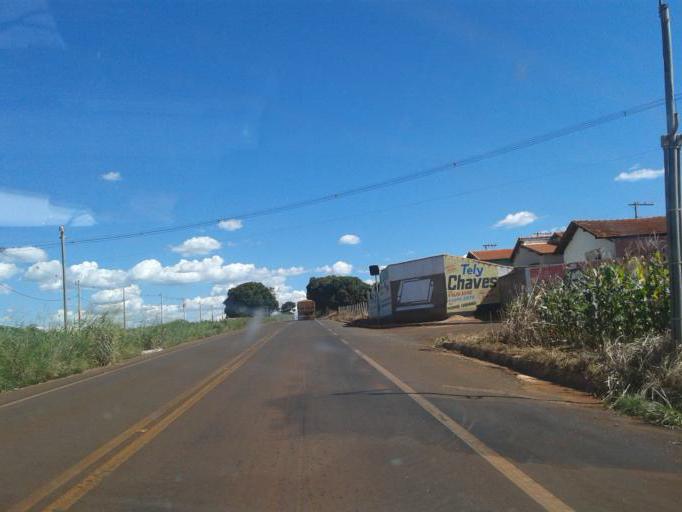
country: BR
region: Minas Gerais
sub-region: Capinopolis
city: Capinopolis
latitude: -18.6824
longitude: -49.5642
